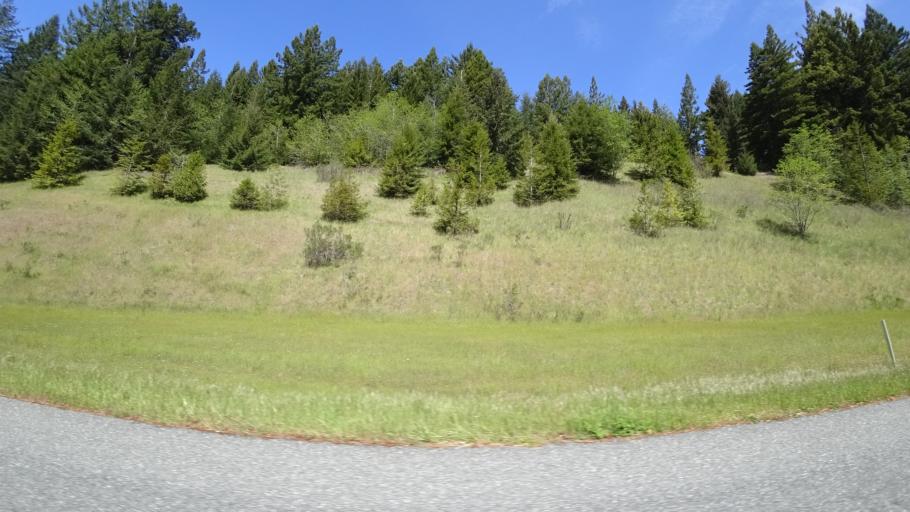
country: US
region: California
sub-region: Humboldt County
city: Westhaven-Moonstone
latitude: 41.3578
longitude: -124.0121
